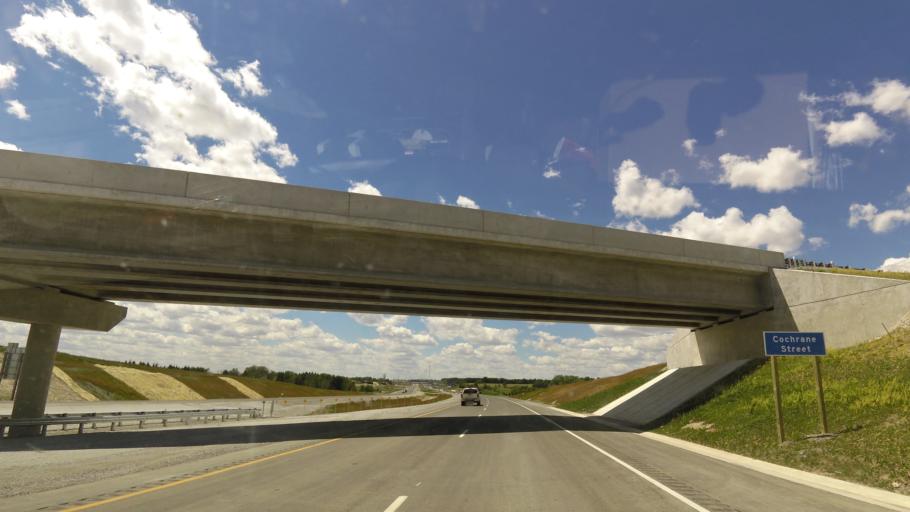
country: CA
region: Ontario
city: Ajax
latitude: 43.9515
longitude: -78.9837
